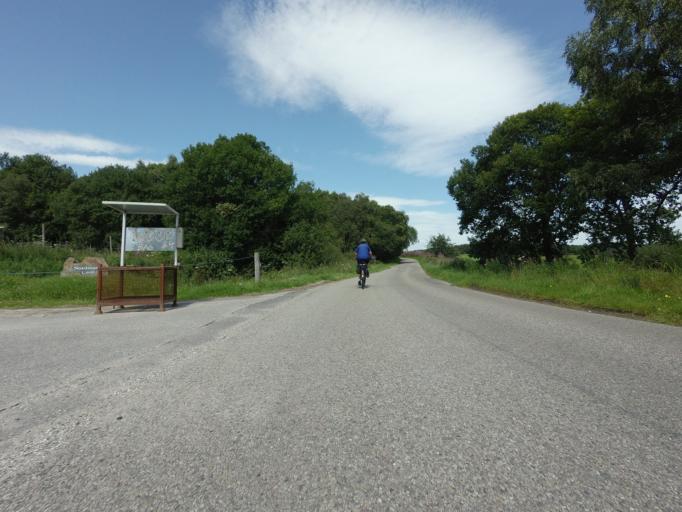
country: GB
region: Scotland
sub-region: Highland
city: Inverness
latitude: 57.5158
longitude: -4.2895
